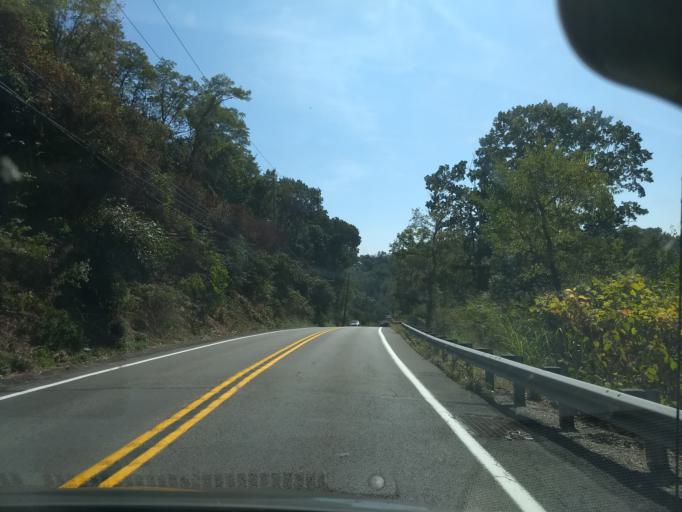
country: US
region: Pennsylvania
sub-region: Allegheny County
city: North Versailles
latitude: 40.3654
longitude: -79.8275
